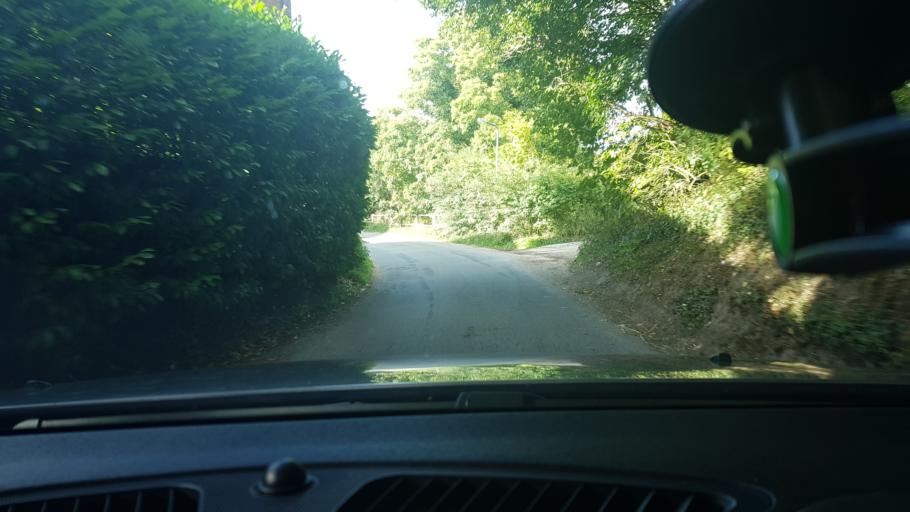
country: GB
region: England
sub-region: Wiltshire
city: Shalbourne
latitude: 51.3706
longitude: -1.5469
